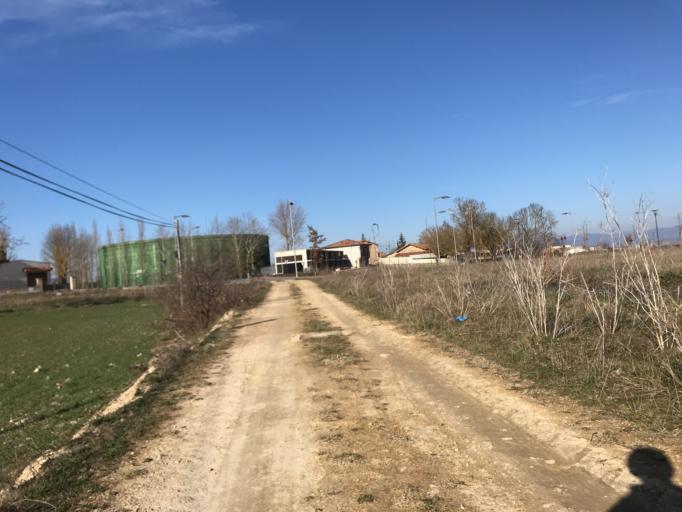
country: ES
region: Basque Country
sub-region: Provincia de Alava
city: Gasteiz / Vitoria
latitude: 42.8208
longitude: -2.6785
